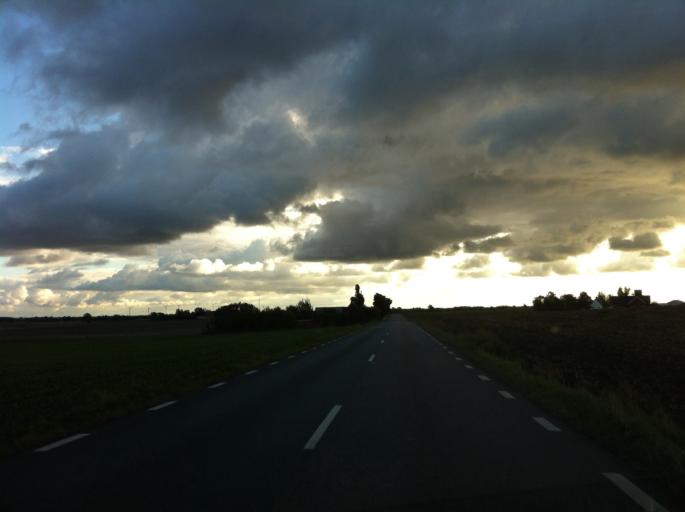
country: SE
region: Skane
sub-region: Svalovs Kommun
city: Svaloev
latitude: 55.8910
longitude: 13.1789
